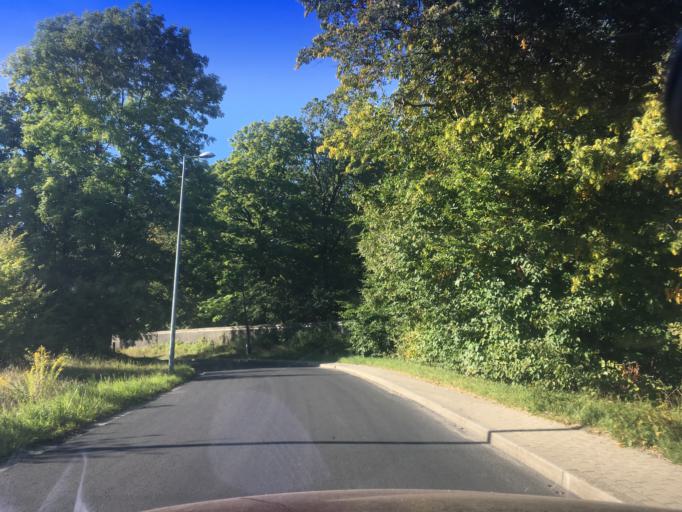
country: PL
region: Lower Silesian Voivodeship
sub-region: Powiat lubanski
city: Swieradow-Zdroj
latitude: 50.9355
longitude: 15.3018
